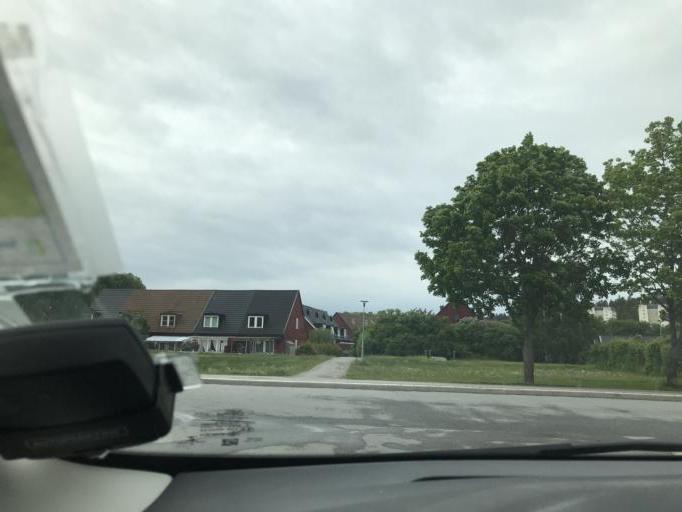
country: SE
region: Stockholm
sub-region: Botkyrka Kommun
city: Tumba
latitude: 59.2023
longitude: 17.8280
